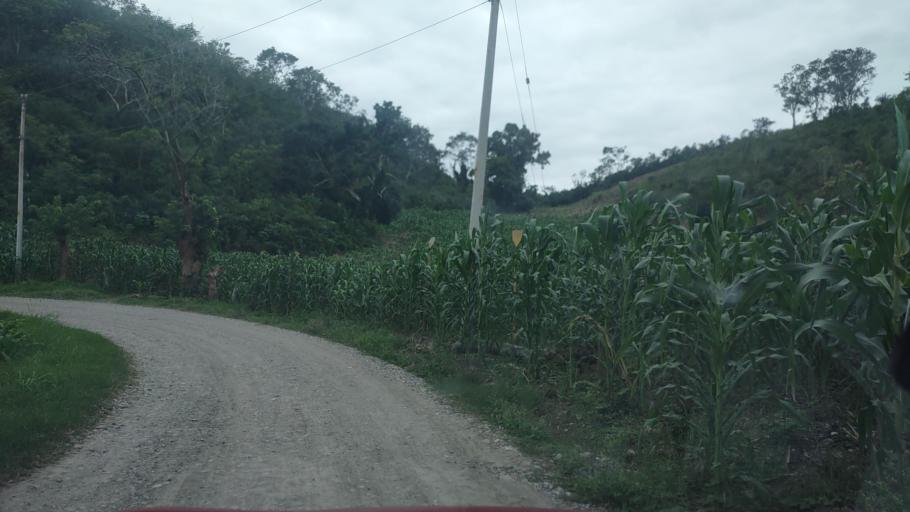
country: MX
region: Veracruz
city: Agua Dulce
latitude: 20.4201
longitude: -97.2688
